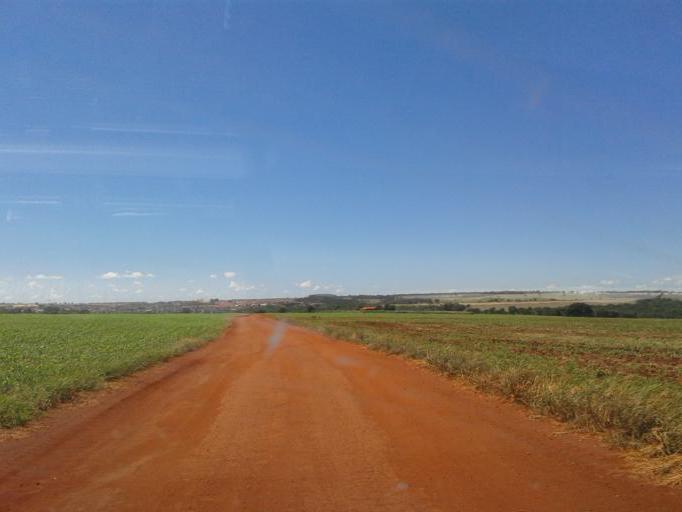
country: BR
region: Minas Gerais
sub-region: Capinopolis
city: Capinopolis
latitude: -18.6583
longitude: -49.6027
